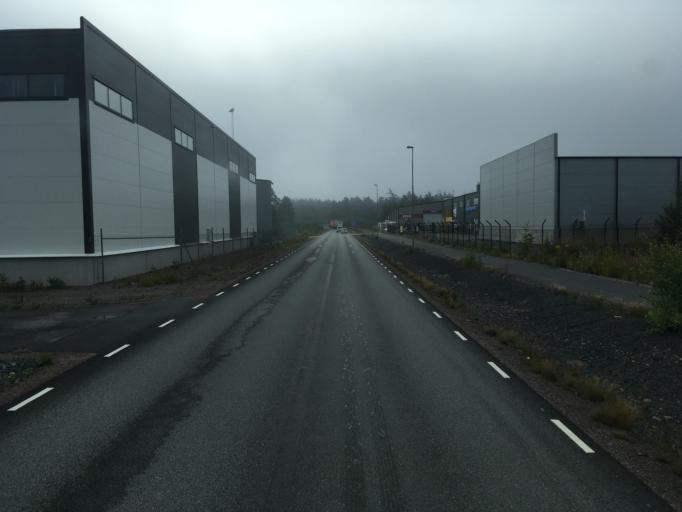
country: SE
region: Joenkoeping
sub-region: Jonkopings Kommun
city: Jonkoping
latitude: 57.7645
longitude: 14.0941
